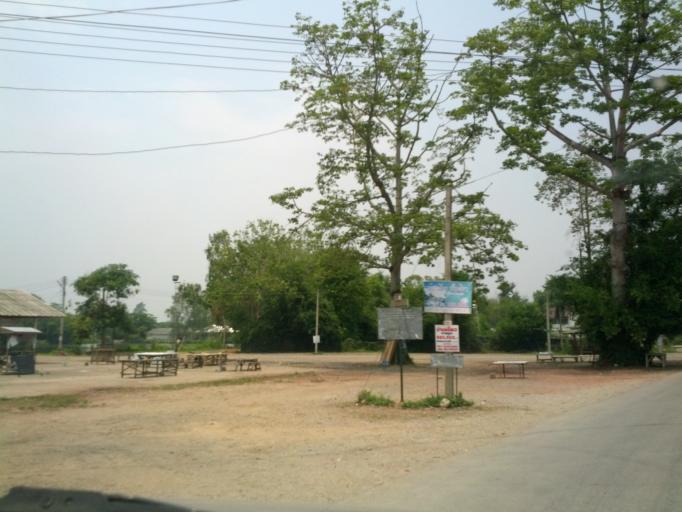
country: TH
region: Chiang Mai
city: San Sai
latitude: 18.8947
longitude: 99.0335
